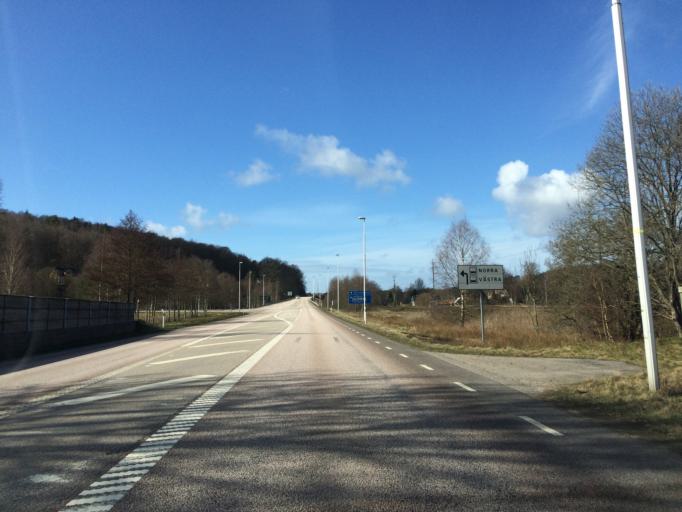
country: SE
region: Halland
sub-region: Laholms Kommun
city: Knared
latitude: 56.5119
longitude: 13.3242
